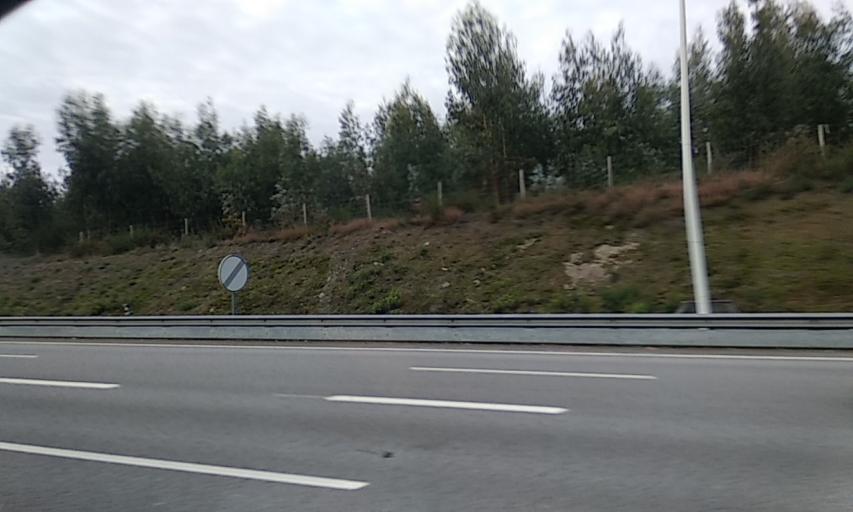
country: PT
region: Porto
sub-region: Valongo
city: Ermesinde
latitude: 41.2345
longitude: -8.5658
